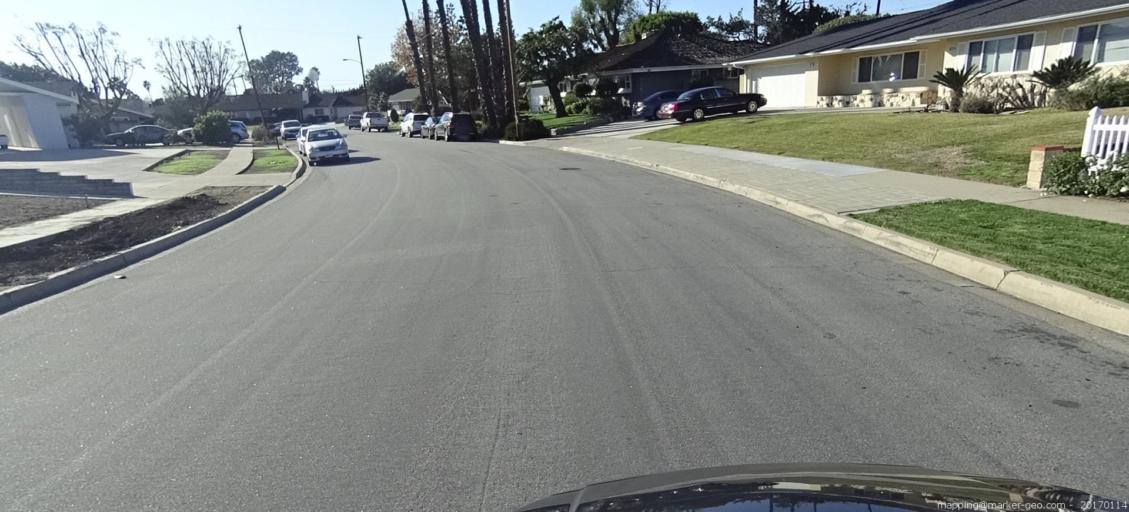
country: US
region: California
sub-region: Orange County
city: North Tustin
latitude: 33.7655
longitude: -117.8128
